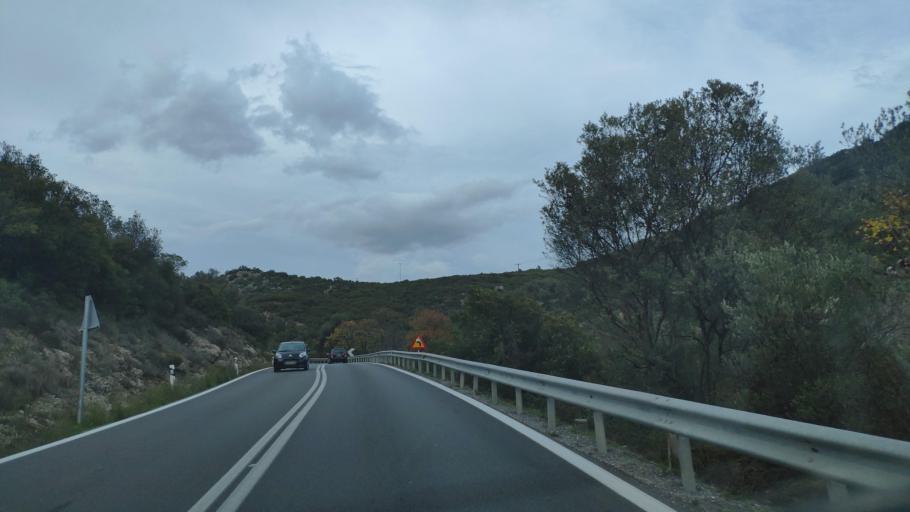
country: GR
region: Peloponnese
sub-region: Nomos Korinthias
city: Ayios Vasilios
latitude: 37.7673
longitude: 22.7280
